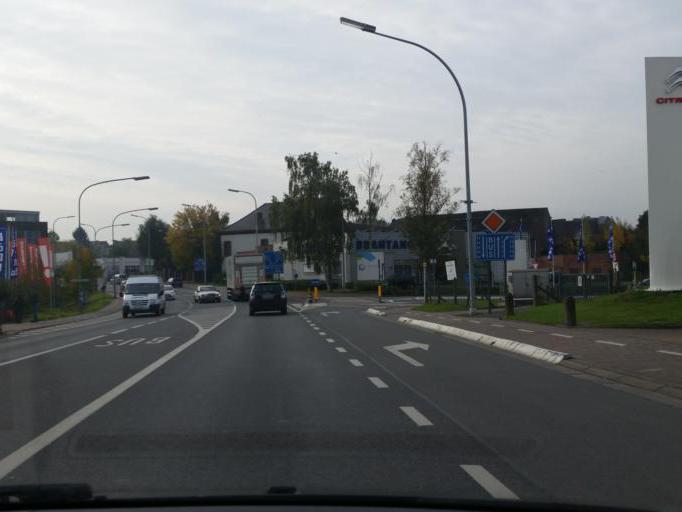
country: BE
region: Flanders
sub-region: Provincie Vlaams-Brabant
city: Halle
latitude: 50.7339
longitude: 4.2296
